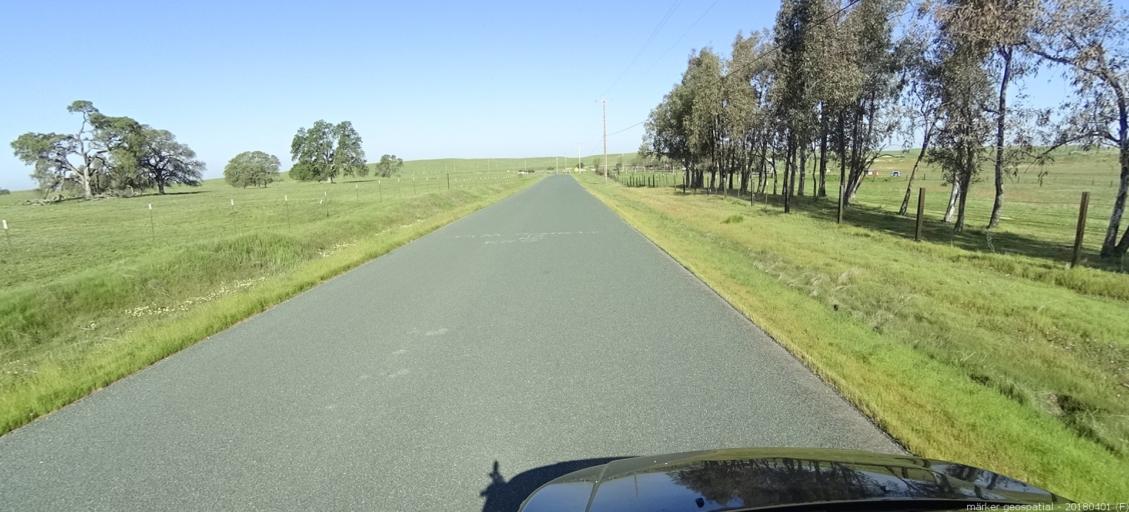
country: US
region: California
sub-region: Sacramento County
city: Rancho Murieta
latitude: 38.4299
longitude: -121.0593
